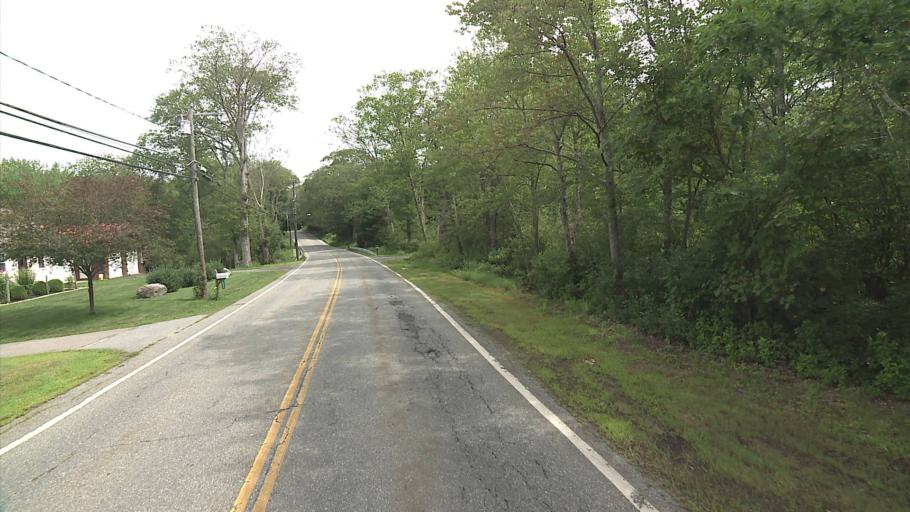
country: US
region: Connecticut
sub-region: Windham County
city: Thompson
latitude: 41.9682
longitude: -71.8552
